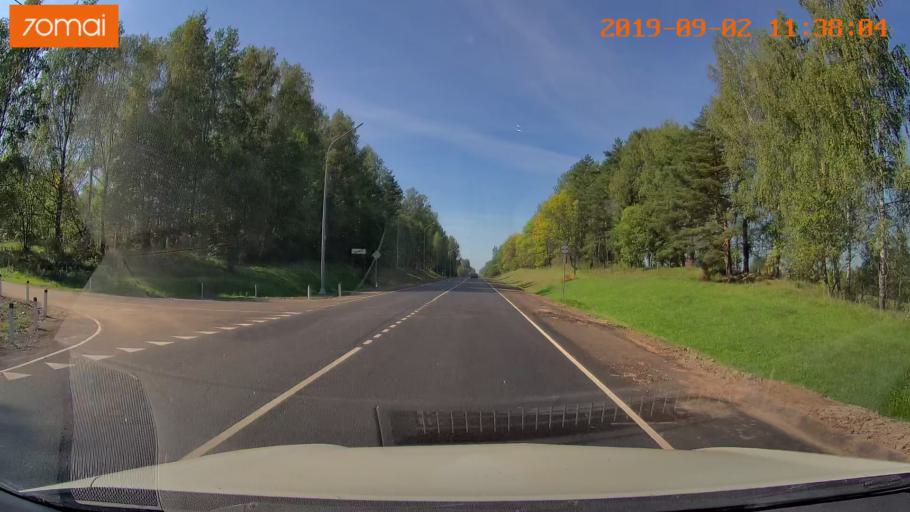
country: RU
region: Smolensk
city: Oster
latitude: 53.9153
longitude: 32.7473
